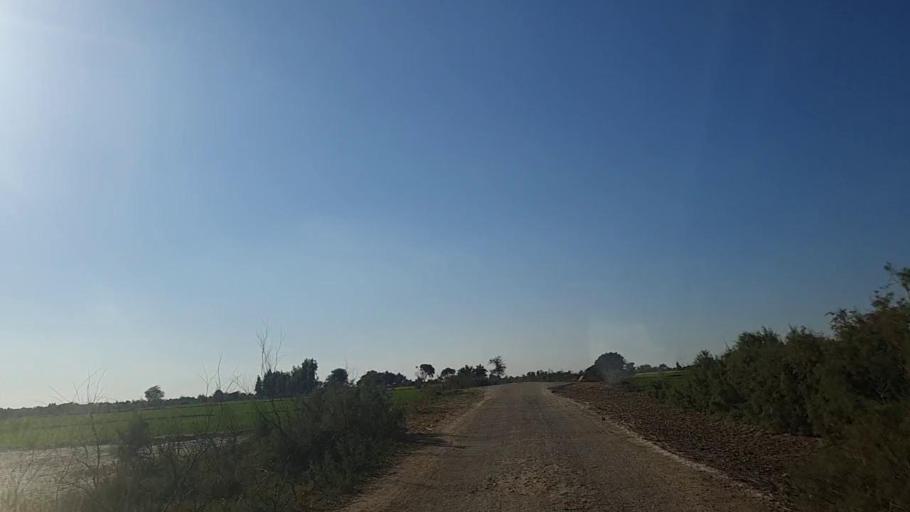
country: PK
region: Sindh
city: Khadro
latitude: 26.2421
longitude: 68.8942
